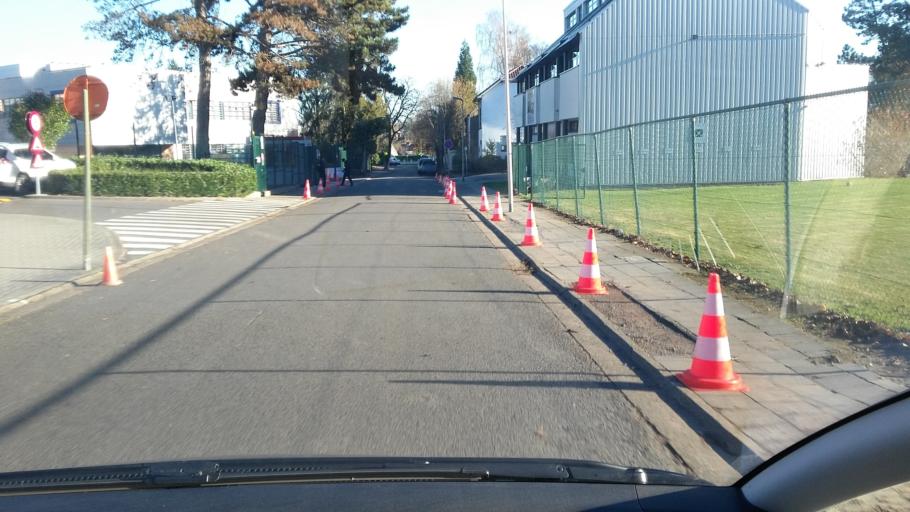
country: BE
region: Wallonia
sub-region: Province du Brabant Wallon
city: Waterloo
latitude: 50.7040
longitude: 4.4140
